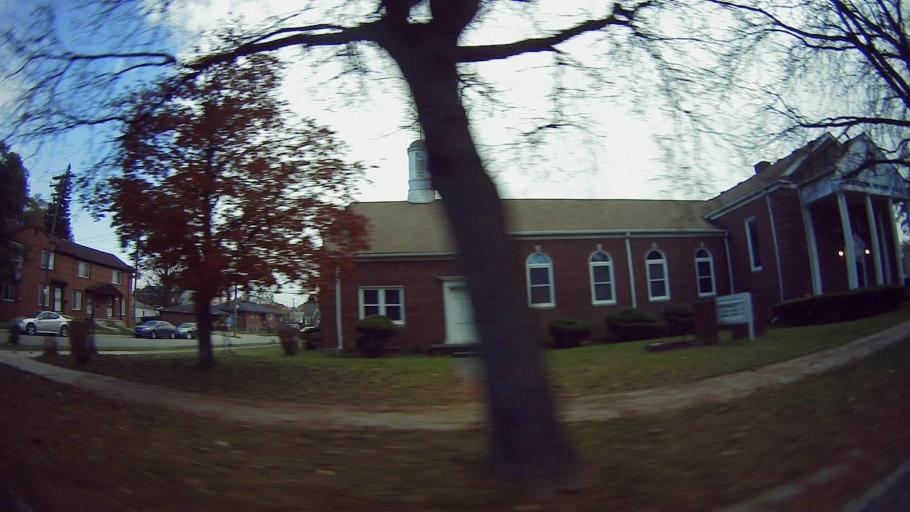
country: US
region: Michigan
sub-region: Wayne County
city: Dearborn
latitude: 42.3536
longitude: -83.1772
